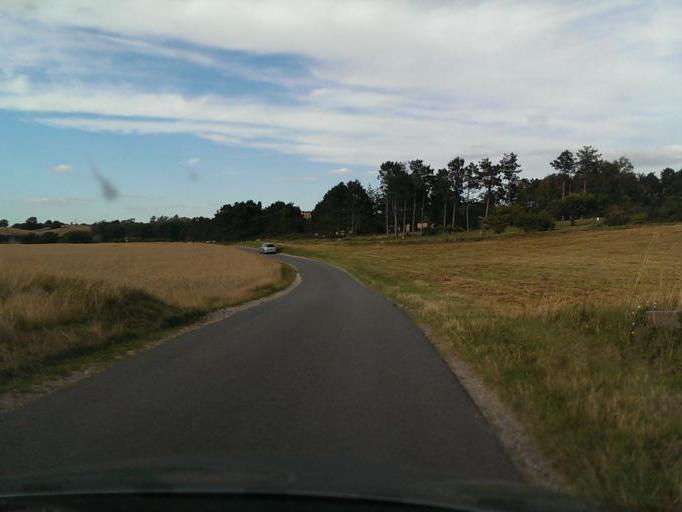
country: DK
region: Central Jutland
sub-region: Syddjurs Kommune
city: Ronde
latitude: 56.1114
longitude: 10.5061
